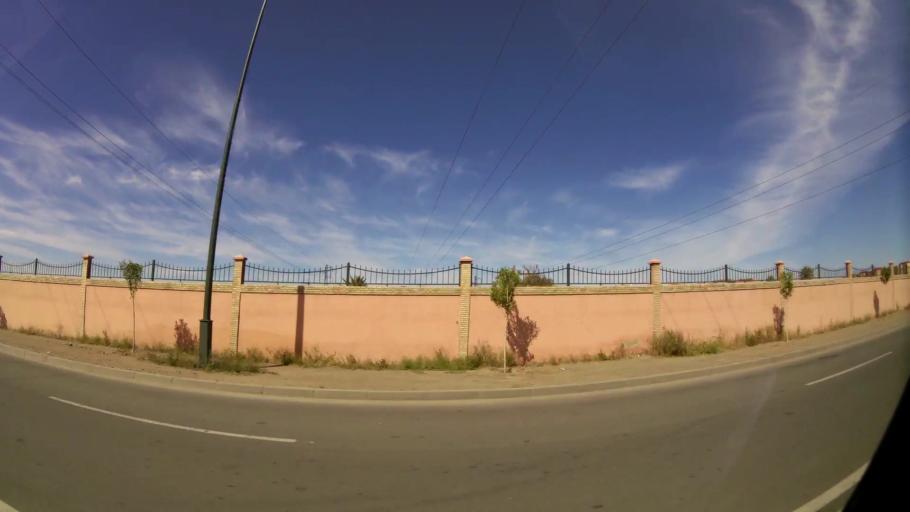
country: MA
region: Marrakech-Tensift-Al Haouz
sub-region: Marrakech
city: Marrakesh
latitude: 31.6605
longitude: -8.0268
